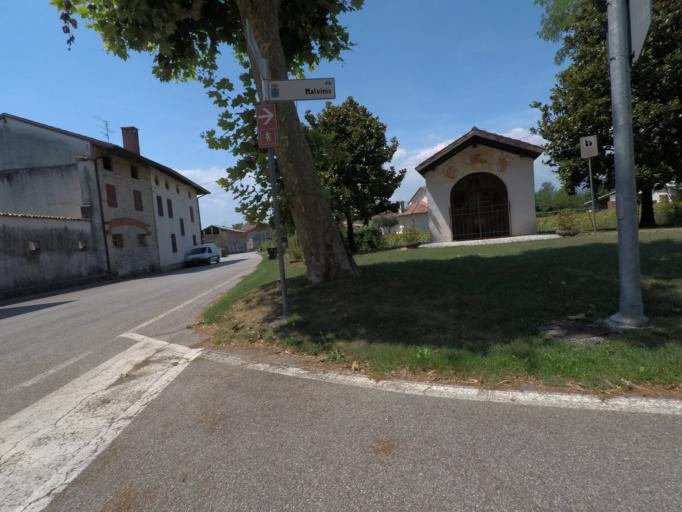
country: IT
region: Friuli Venezia Giulia
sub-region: Provincia di Pordenone
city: Lestans
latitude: 46.1404
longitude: 12.9086
